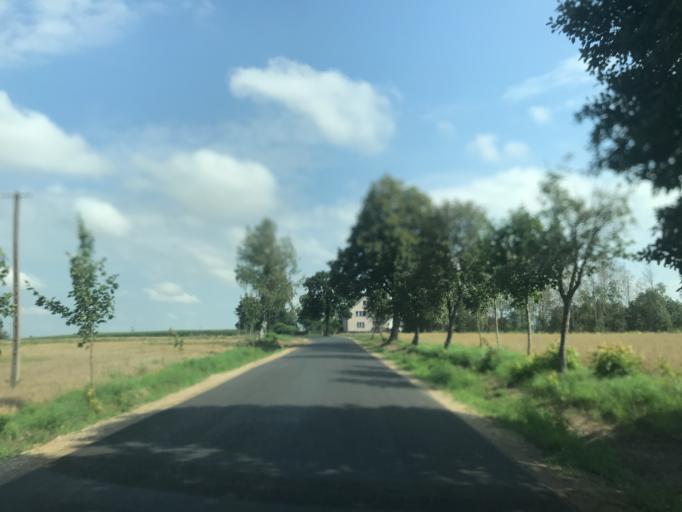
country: PL
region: Warmian-Masurian Voivodeship
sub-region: Powiat nowomiejski
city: Kurzetnik
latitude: 53.3888
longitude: 19.4684
